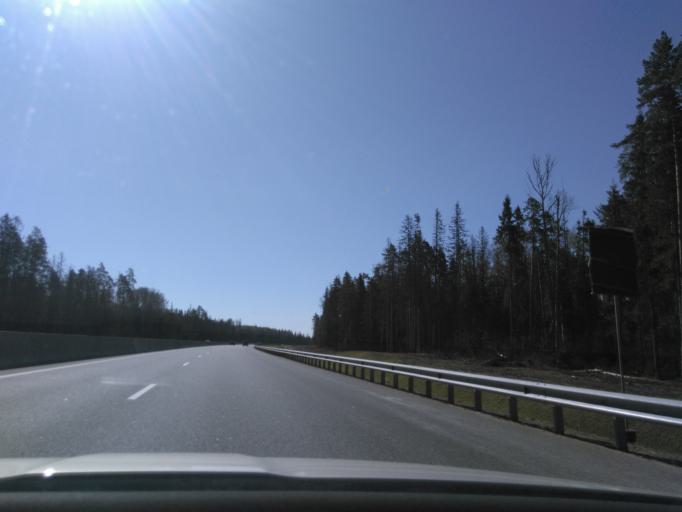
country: RU
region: Moskovskaya
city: Mendeleyevo
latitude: 56.0545
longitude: 37.2534
